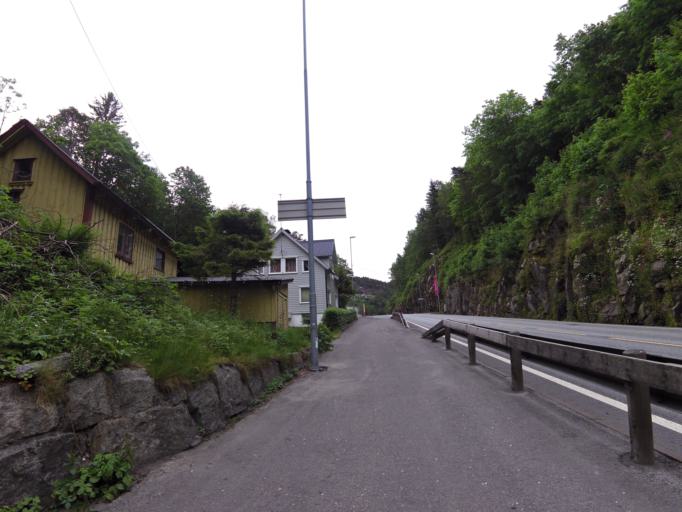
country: NO
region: Vest-Agder
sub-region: Flekkefjord
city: Flekkefjord
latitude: 58.2971
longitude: 6.6722
